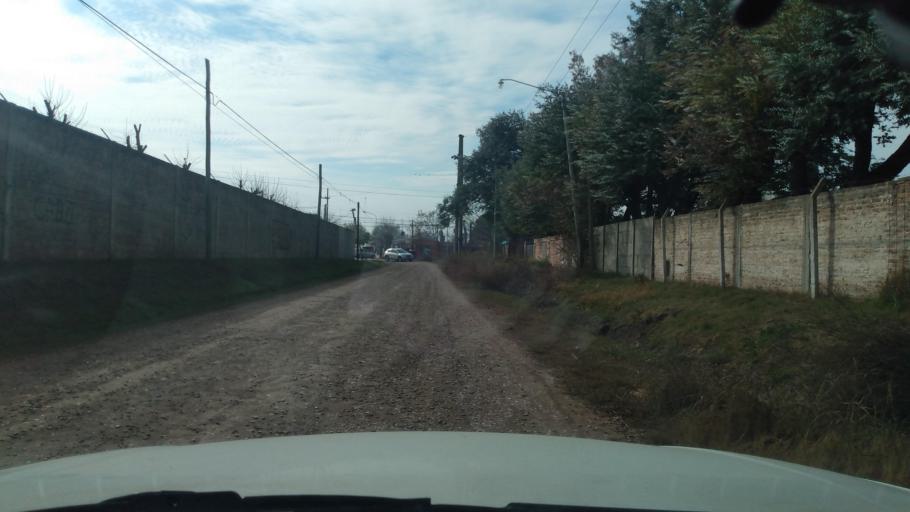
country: AR
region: Buenos Aires
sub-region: Partido de Lujan
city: Lujan
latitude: -34.5850
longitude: -59.1188
